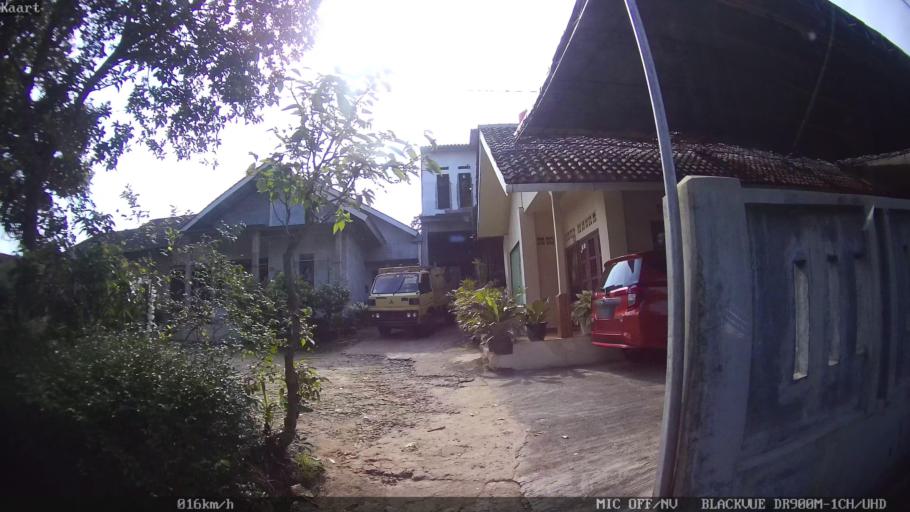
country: ID
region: Lampung
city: Kedaton
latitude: -5.3925
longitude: 105.2218
